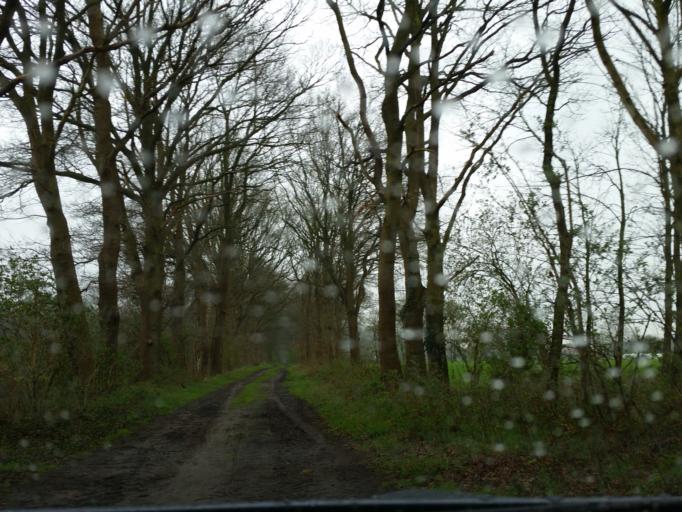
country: DE
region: Lower Saxony
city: Hipstedt
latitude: 53.4873
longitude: 8.9599
